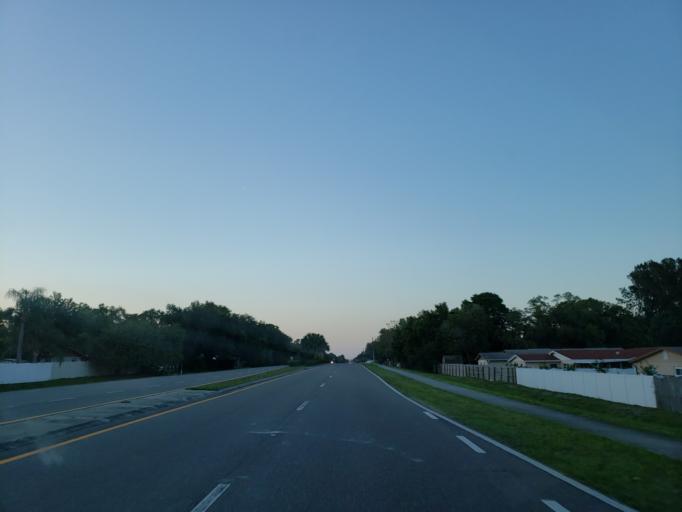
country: US
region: Florida
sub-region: Pinellas County
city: Ridgecrest
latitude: 27.8734
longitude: -82.7952
